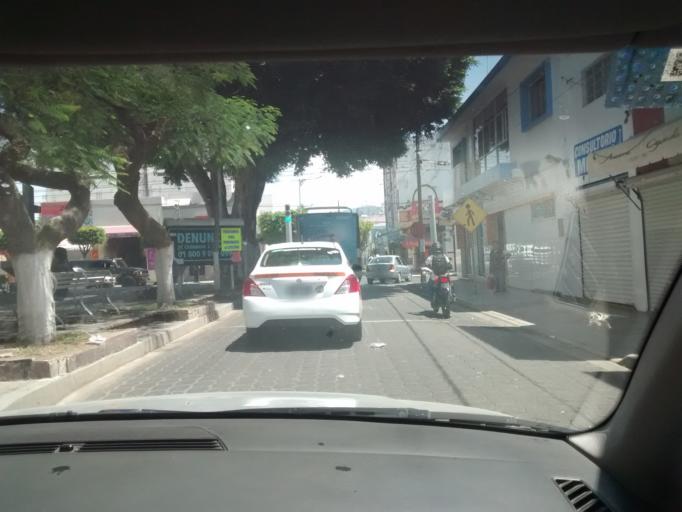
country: MX
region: Puebla
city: Tehuacan
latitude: 18.4584
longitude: -97.3925
